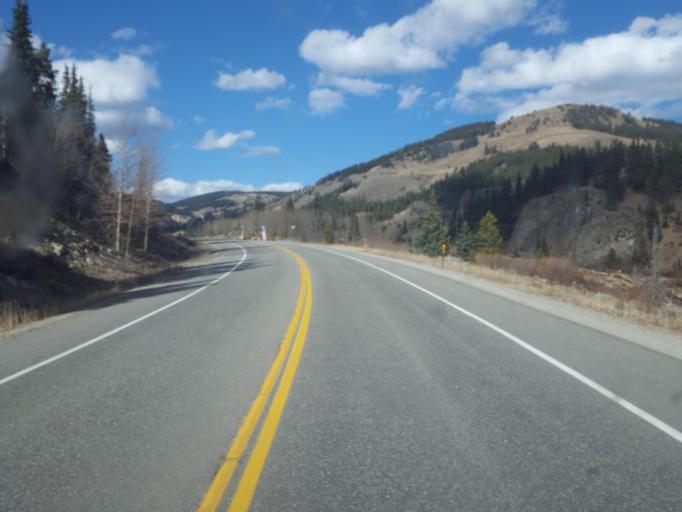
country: US
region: Colorado
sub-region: Lake County
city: Leadville
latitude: 39.3274
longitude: -106.2194
